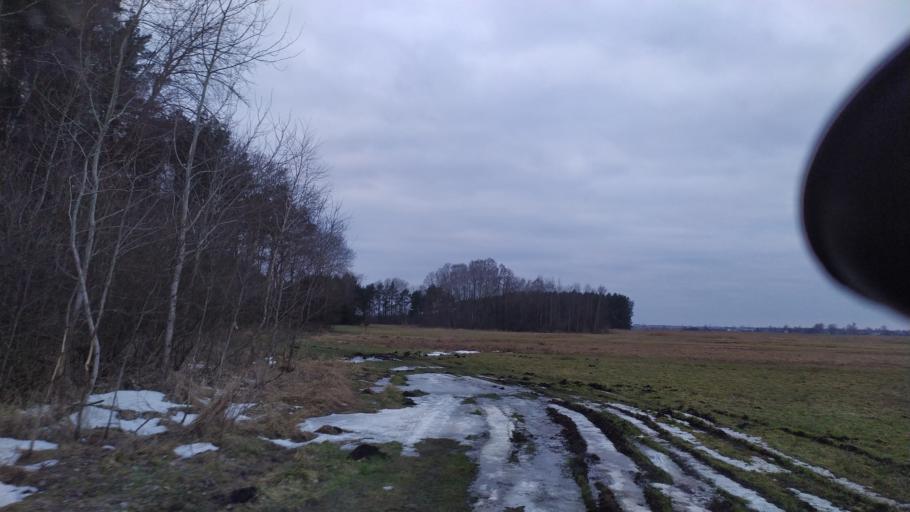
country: PL
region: Lublin Voivodeship
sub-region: Powiat lubartowski
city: Abramow
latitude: 51.4302
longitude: 22.2914
